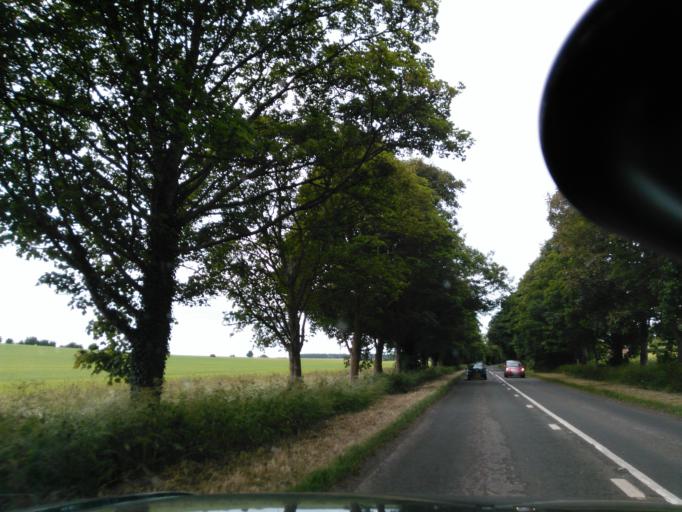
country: GB
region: England
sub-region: Wiltshire
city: Market Lavington
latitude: 51.2482
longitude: -1.9818
